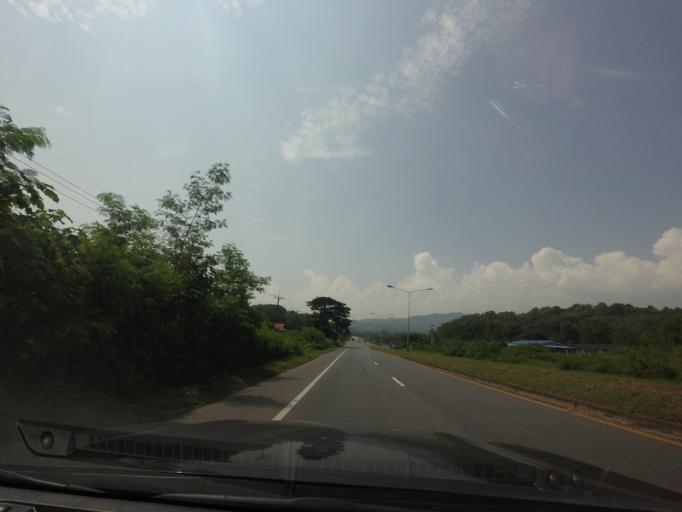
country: TH
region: Phrae
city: Den Chai
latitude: 17.9440
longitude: 100.0648
